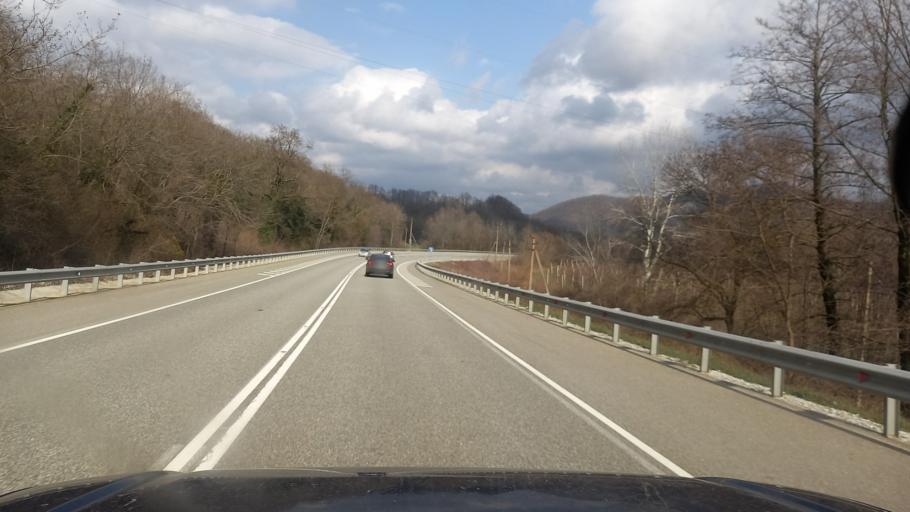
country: RU
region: Krasnodarskiy
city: Pshada
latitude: 44.4576
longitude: 38.3550
